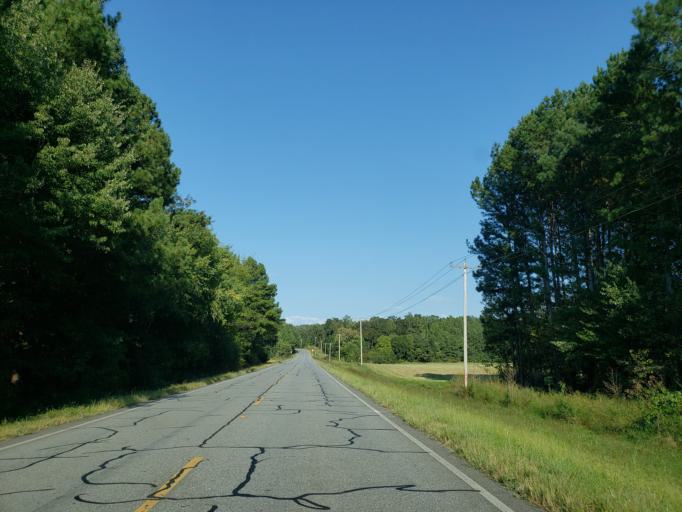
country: US
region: Georgia
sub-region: Whitfield County
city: Varnell
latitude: 34.9080
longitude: -84.8747
